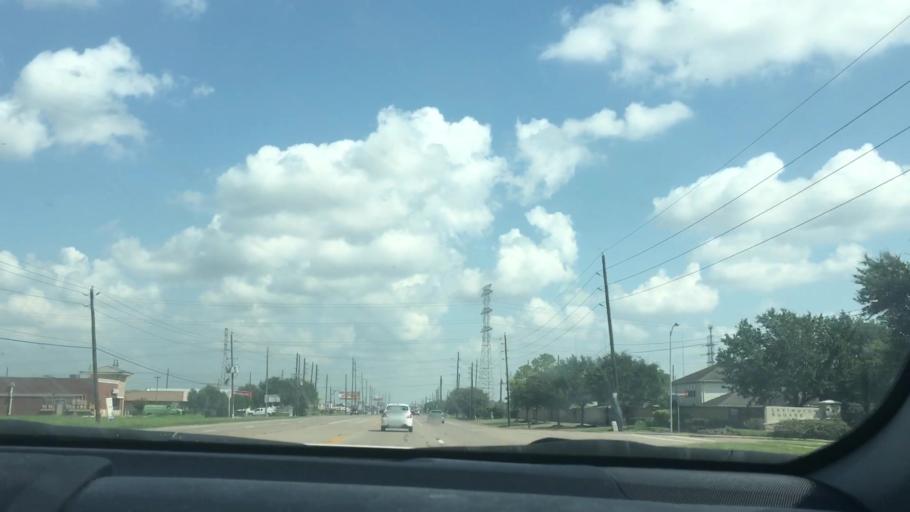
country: US
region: Texas
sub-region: Fort Bend County
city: Fifth Street
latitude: 29.6022
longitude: -95.5643
